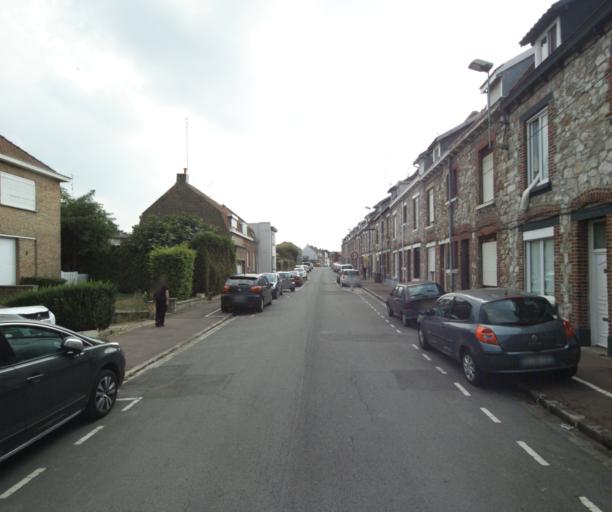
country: FR
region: Nord-Pas-de-Calais
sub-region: Departement du Nord
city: Tourcoing
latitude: 50.7291
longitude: 3.1408
